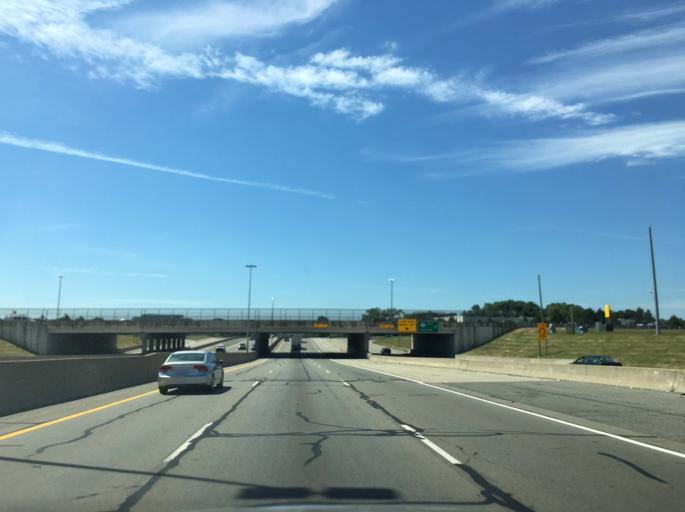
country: US
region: Michigan
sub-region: Wayne County
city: Dearborn
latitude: 42.3304
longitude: -83.2159
